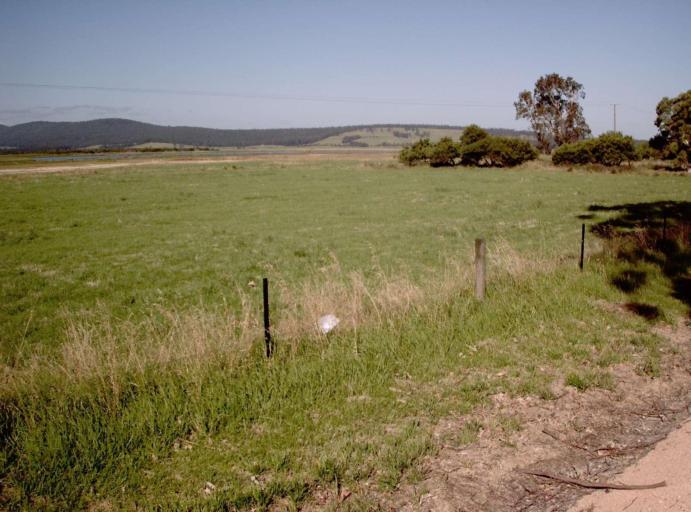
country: AU
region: Victoria
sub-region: East Gippsland
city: Lakes Entrance
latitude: -37.7576
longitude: 148.5328
